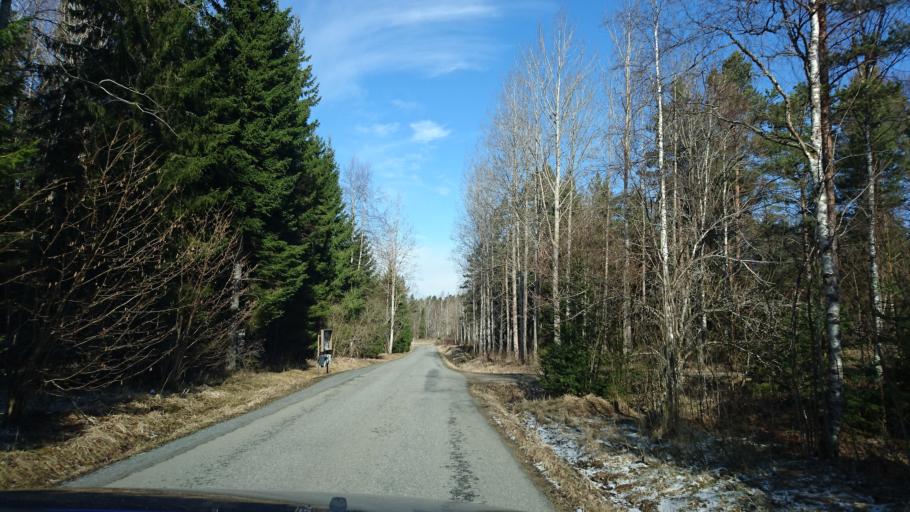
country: SE
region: Stockholm
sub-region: Norrtalje Kommun
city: Bjorko
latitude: 59.7944
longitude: 18.9744
